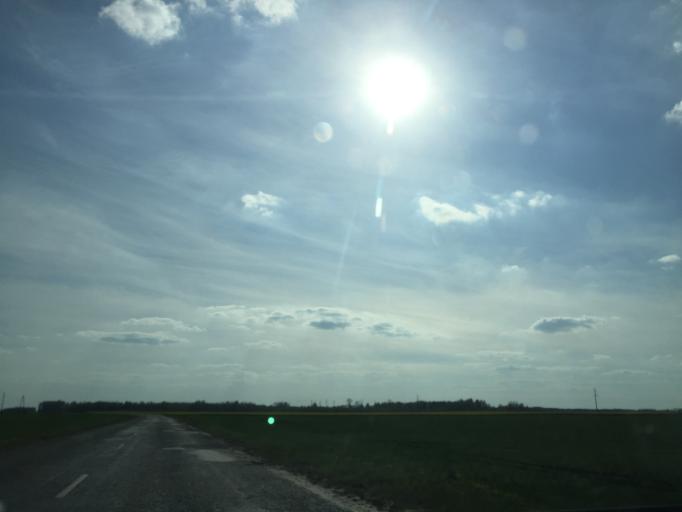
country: LV
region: Bauskas Rajons
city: Bauska
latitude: 56.4768
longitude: 24.3050
